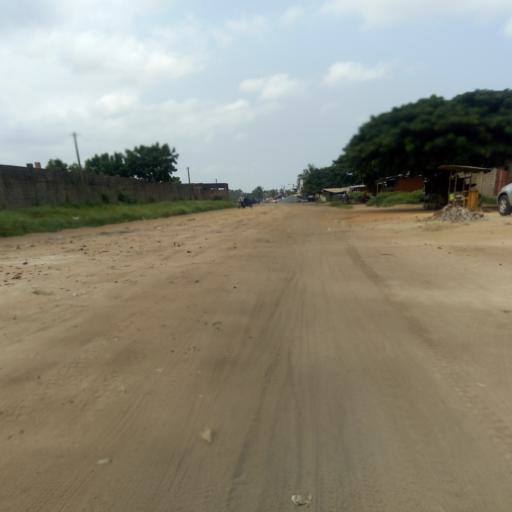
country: TG
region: Maritime
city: Lome
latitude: 6.1858
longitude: 1.1687
